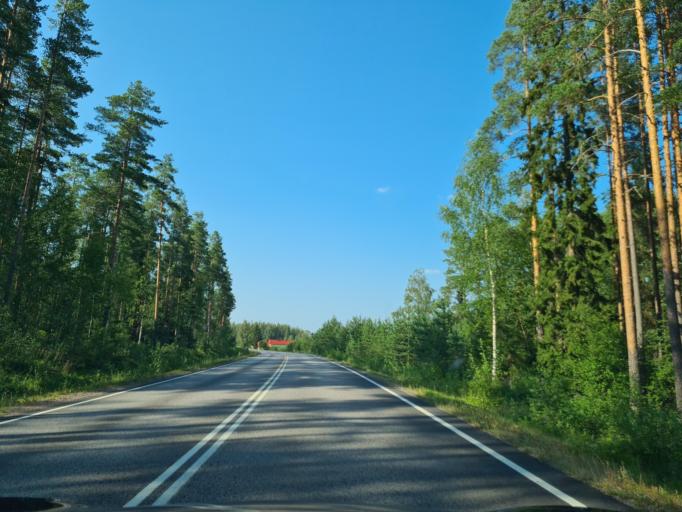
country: FI
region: Satakunta
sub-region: Pohjois-Satakunta
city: Karvia
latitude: 62.2274
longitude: 22.6171
